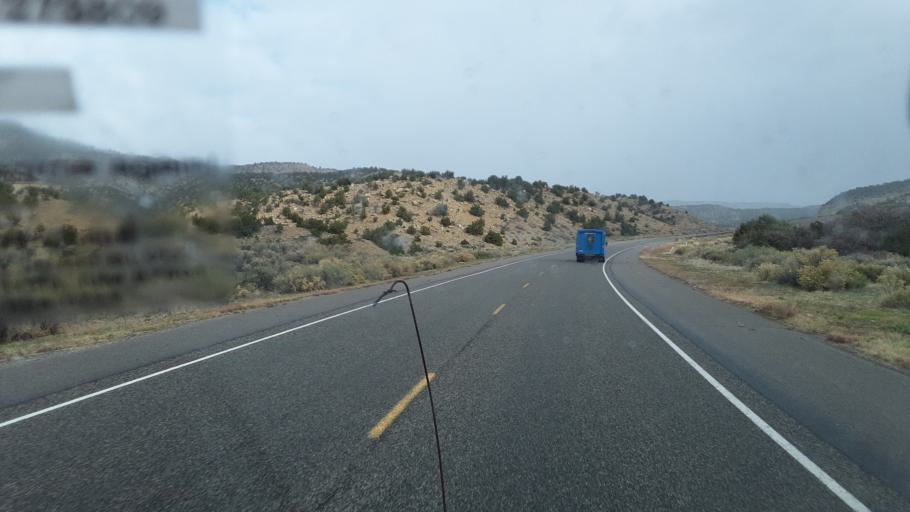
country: US
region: New Mexico
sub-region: Rio Arriba County
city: Santa Teresa
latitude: 36.3715
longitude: -106.5056
